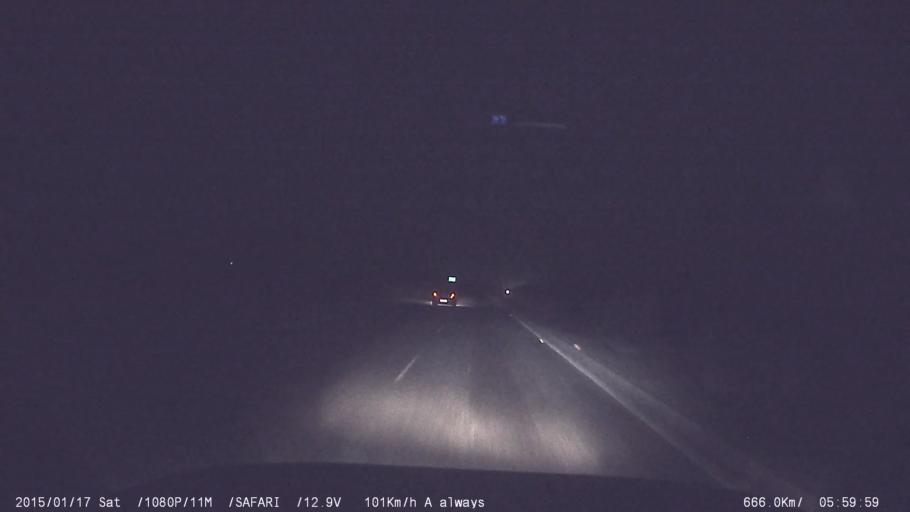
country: IN
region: Tamil Nadu
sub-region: Kancheepuram
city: Kanchipuram
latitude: 12.8967
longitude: 79.5736
